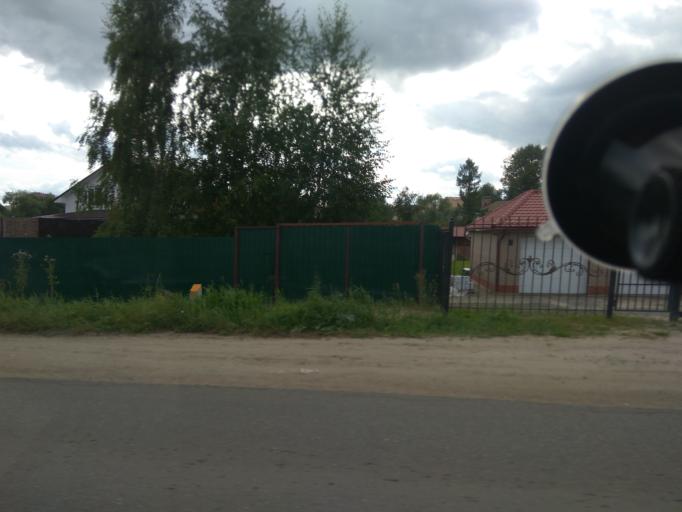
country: RU
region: Moskovskaya
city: Ramenskoye
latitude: 55.5849
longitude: 38.2555
